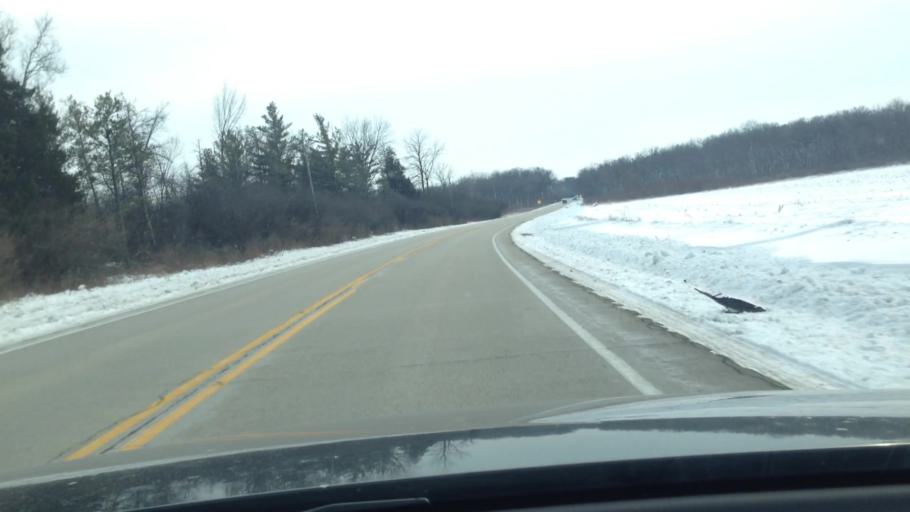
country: US
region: Illinois
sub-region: McHenry County
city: Hebron
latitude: 42.3946
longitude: -88.4388
